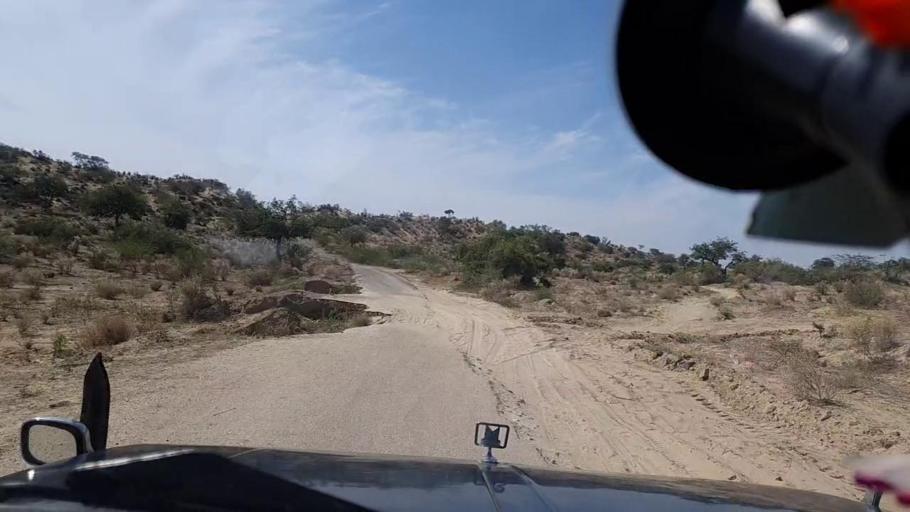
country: PK
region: Sindh
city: Diplo
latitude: 24.4096
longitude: 69.5846
